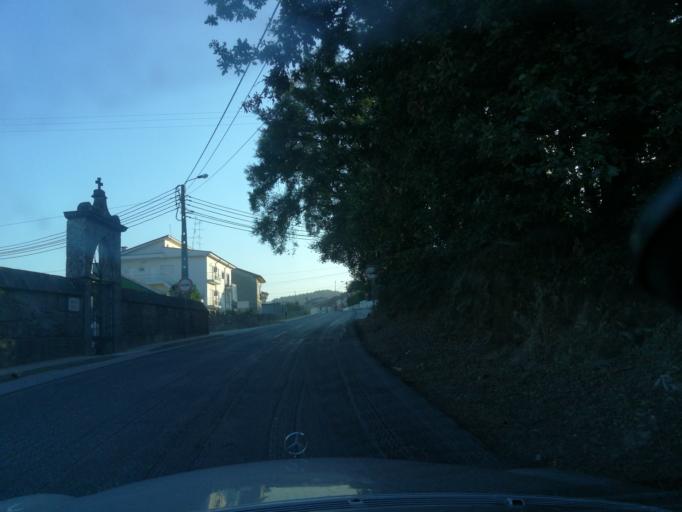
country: PT
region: Braga
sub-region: Braga
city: Braga
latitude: 41.5229
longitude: -8.4318
